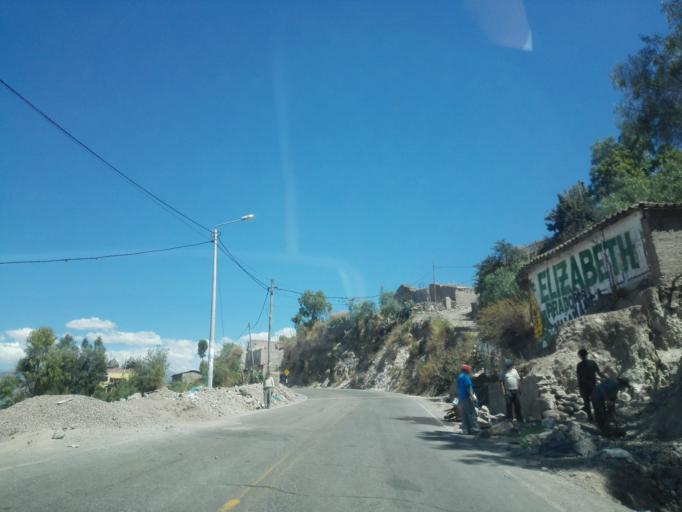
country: PE
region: Ayacucho
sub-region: Provincia de Huamanga
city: Ayacucho
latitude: -13.1642
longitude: -74.2394
